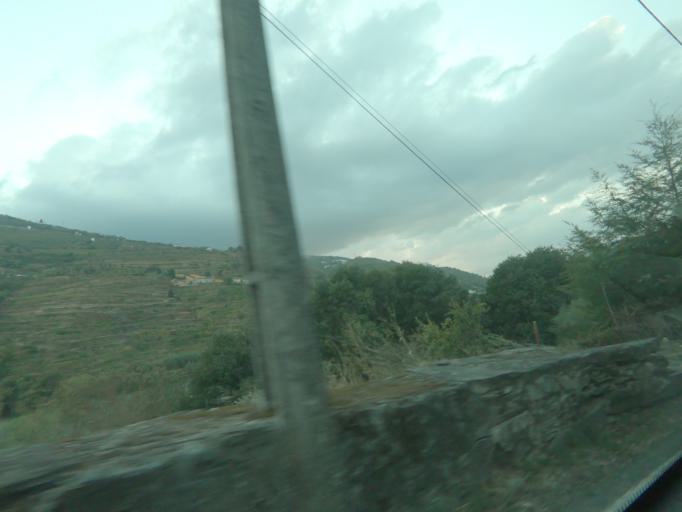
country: PT
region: Vila Real
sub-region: Peso da Regua
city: Godim
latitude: 41.1487
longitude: -7.8200
